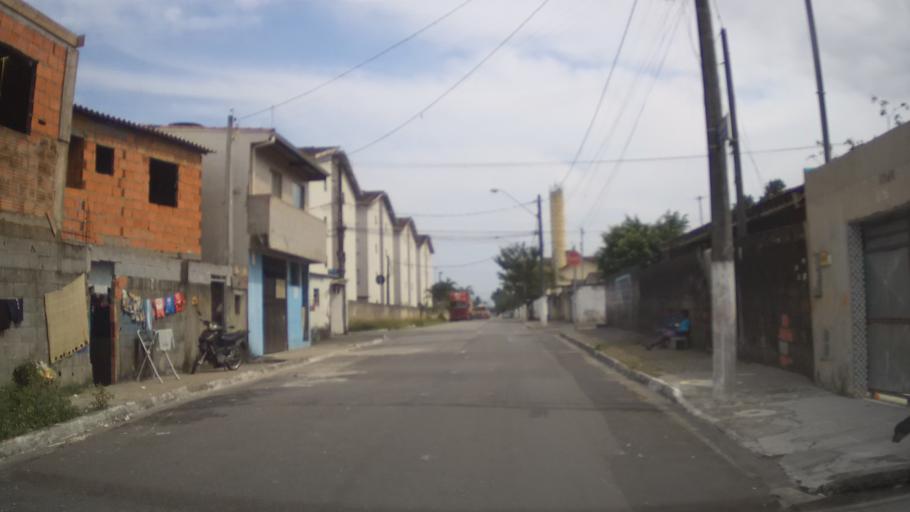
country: BR
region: Sao Paulo
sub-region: Praia Grande
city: Praia Grande
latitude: -23.9957
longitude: -46.4496
